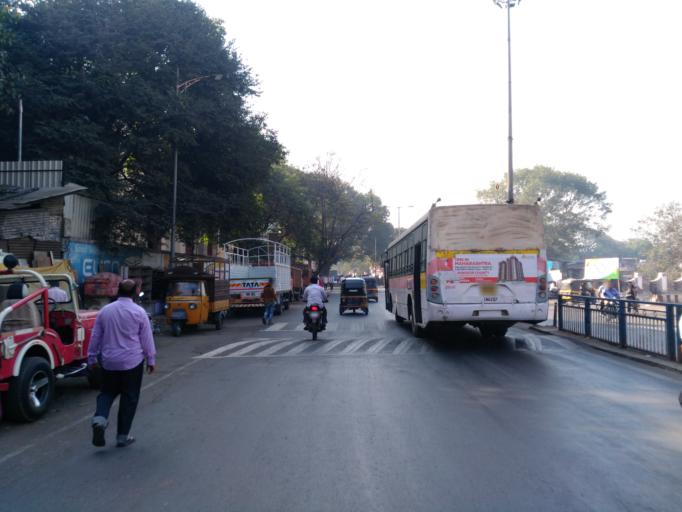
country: IN
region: Maharashtra
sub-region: Pune Division
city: Pune
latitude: 18.5066
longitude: 73.8686
